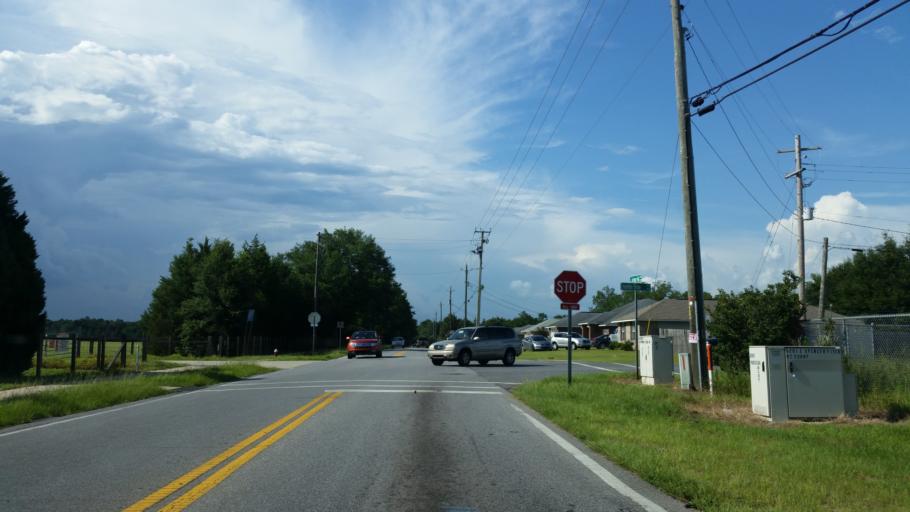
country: US
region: Florida
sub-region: Santa Rosa County
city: Pace
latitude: 30.6248
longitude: -87.1315
